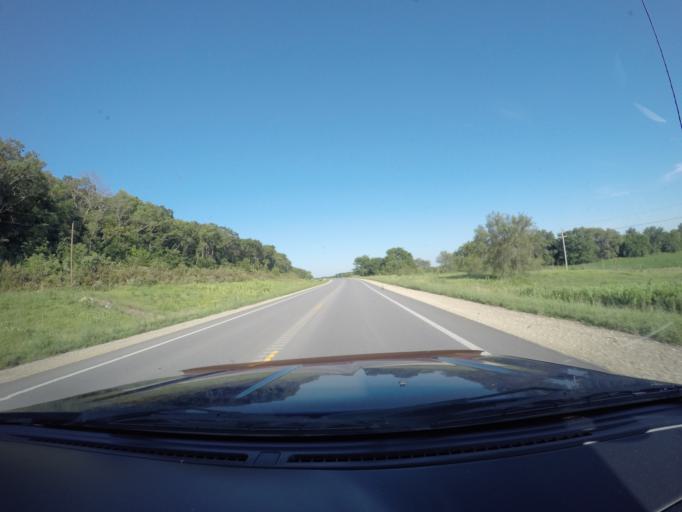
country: US
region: Kansas
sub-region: Jefferson County
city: Oskaloosa
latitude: 39.0703
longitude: -95.3538
